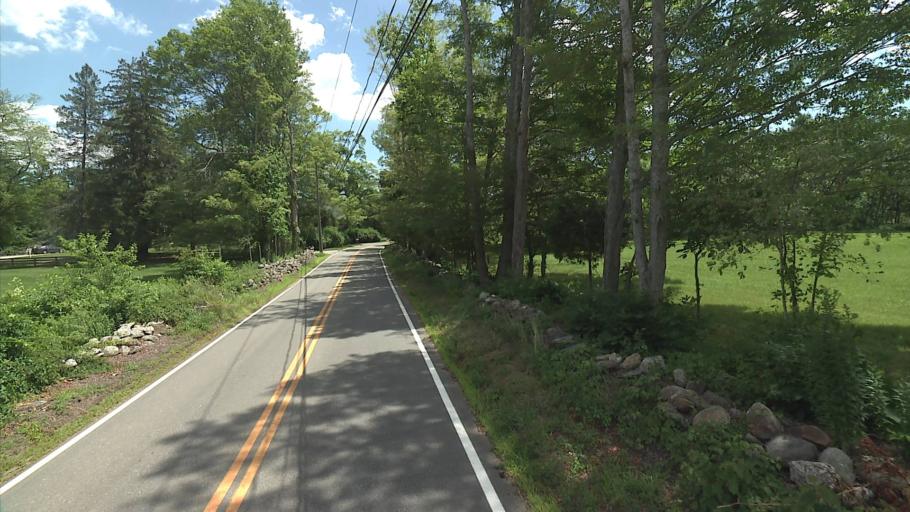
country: US
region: Connecticut
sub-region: New London County
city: Colchester
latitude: 41.4939
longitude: -72.3480
